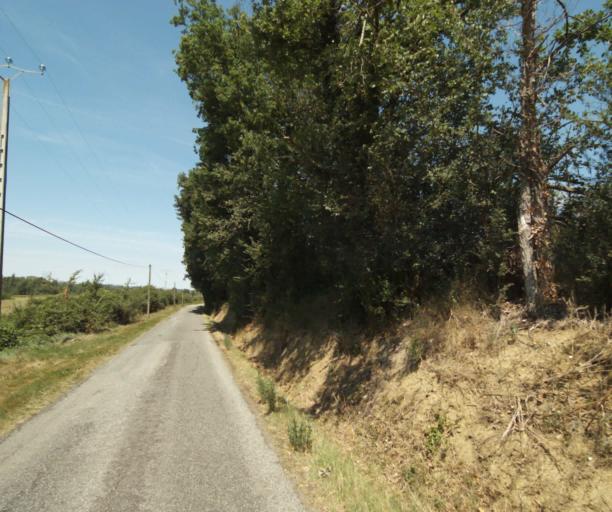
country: FR
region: Midi-Pyrenees
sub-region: Departement de l'Ariege
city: Lezat-sur-Leze
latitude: 43.2941
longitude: 1.3529
